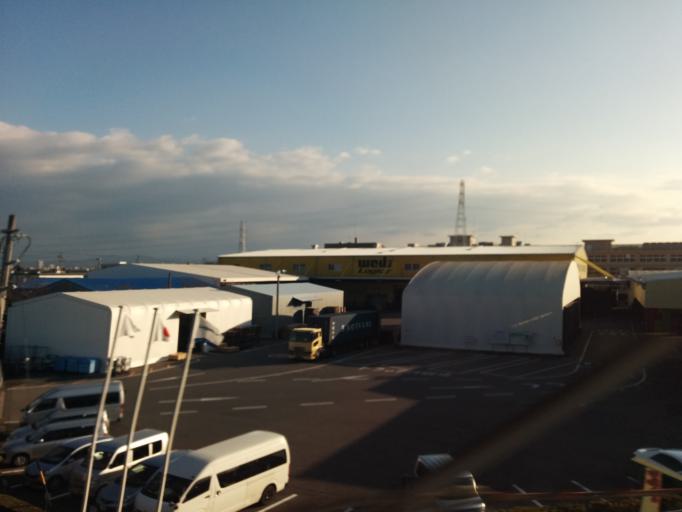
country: JP
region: Aichi
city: Anjo
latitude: 34.9106
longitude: 137.1142
